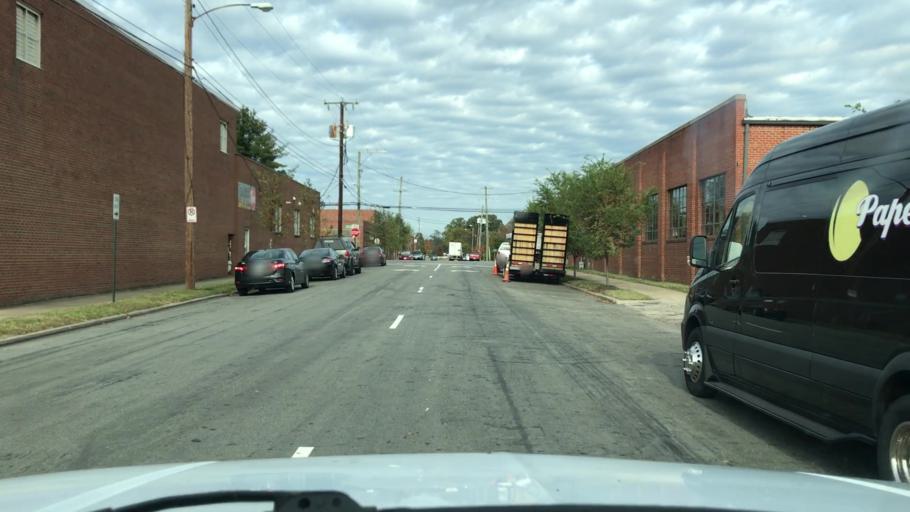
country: US
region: Virginia
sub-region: City of Richmond
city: Richmond
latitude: 37.5707
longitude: -77.4715
